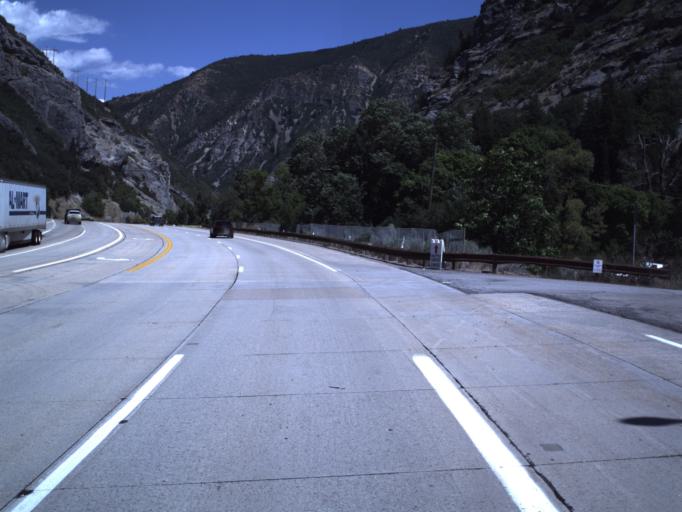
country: US
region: Utah
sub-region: Utah County
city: Orem
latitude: 40.3567
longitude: -111.5718
